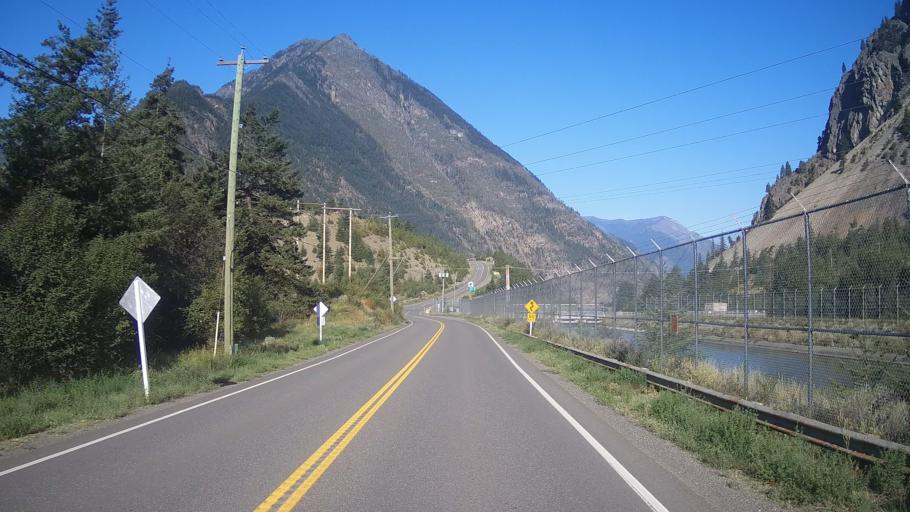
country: CA
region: British Columbia
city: Lillooet
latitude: 50.6692
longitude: -121.9749
